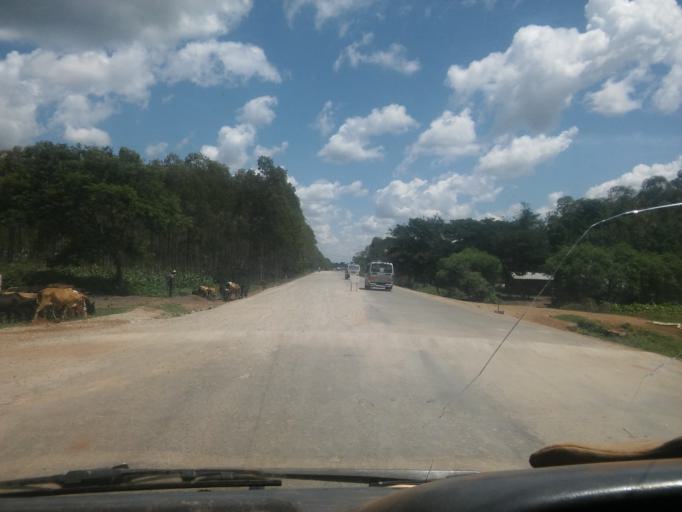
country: UG
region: Eastern Region
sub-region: Mbale District
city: Mbale
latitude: 1.0766
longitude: 34.1379
